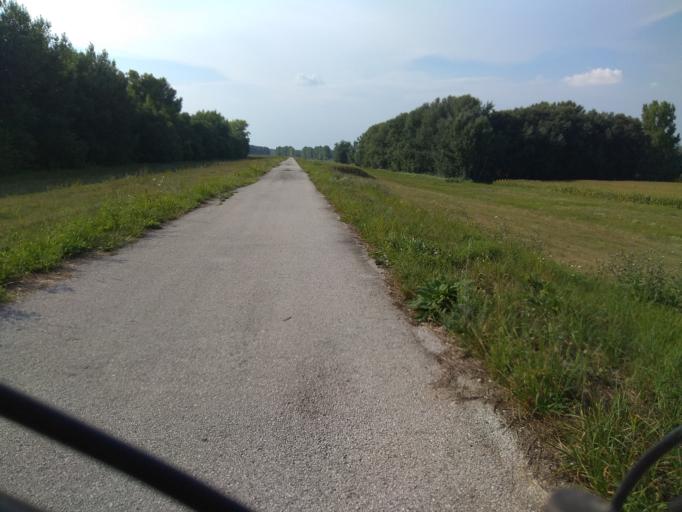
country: SK
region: Trnavsky
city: Gabcikovo
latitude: 47.8010
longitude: 17.6497
